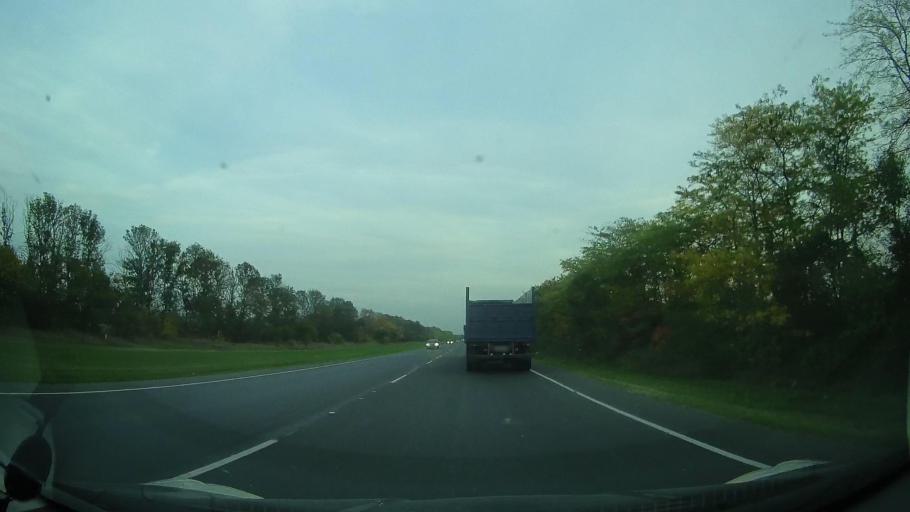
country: RU
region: Rostov
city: Kirovskaya
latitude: 46.9998
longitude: 39.9864
